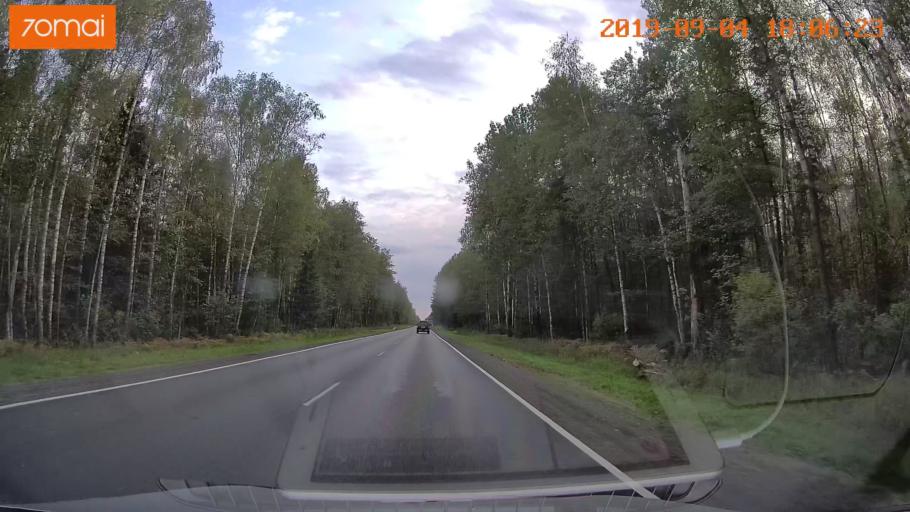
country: RU
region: Moskovskaya
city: Khorlovo
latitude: 55.4318
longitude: 38.8155
